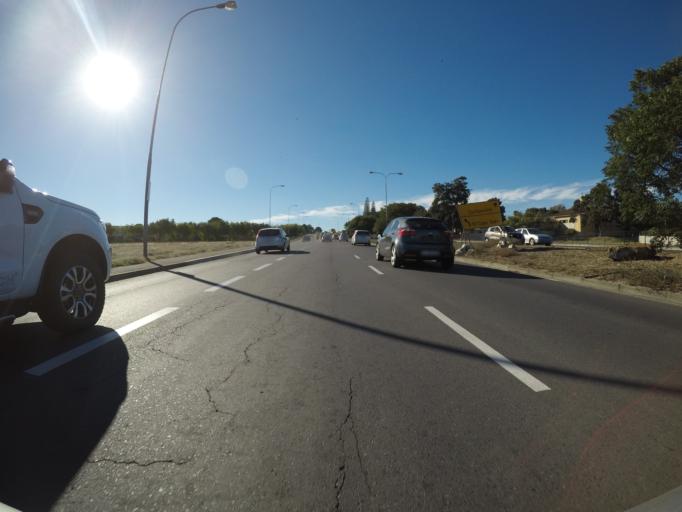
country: ZA
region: Western Cape
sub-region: City of Cape Town
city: Kraaifontein
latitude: -33.8806
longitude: 18.6623
